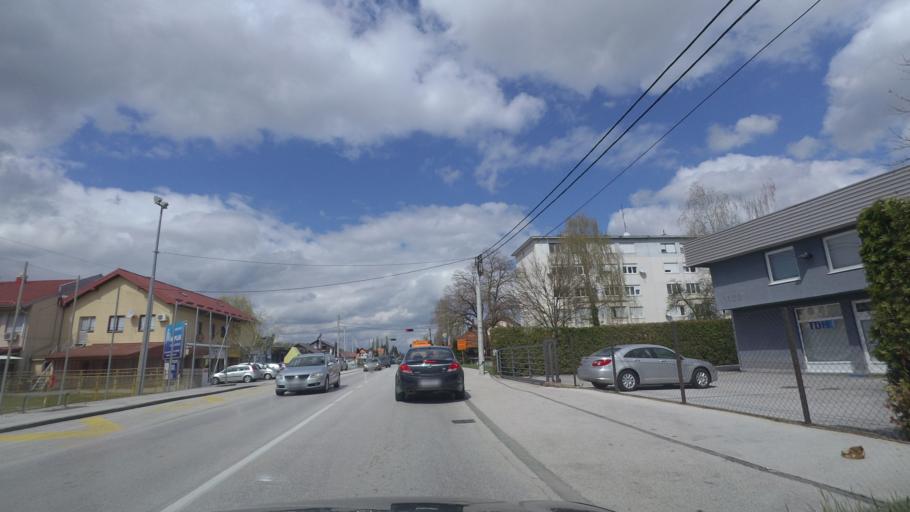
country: HR
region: Zagrebacka
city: Kerestinec
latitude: 45.7680
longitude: 15.8038
